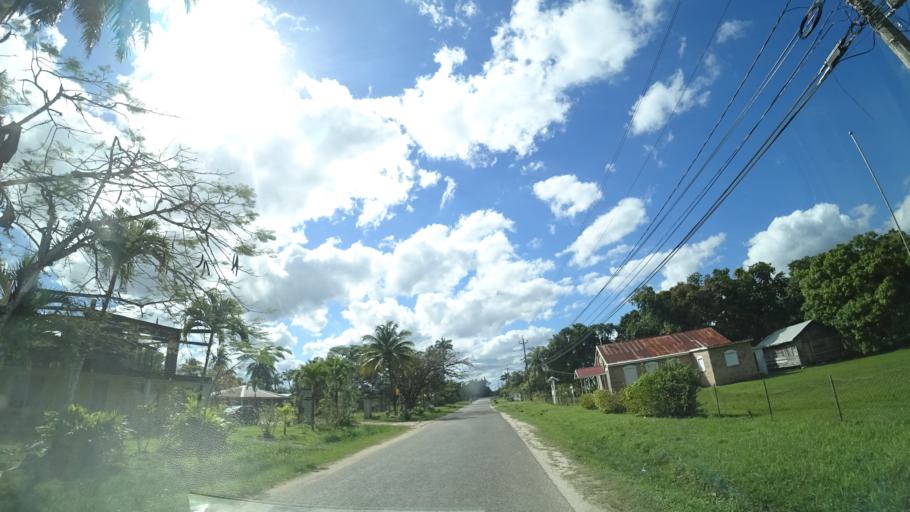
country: BZ
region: Belize
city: Belize City
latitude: 17.5691
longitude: -88.4063
